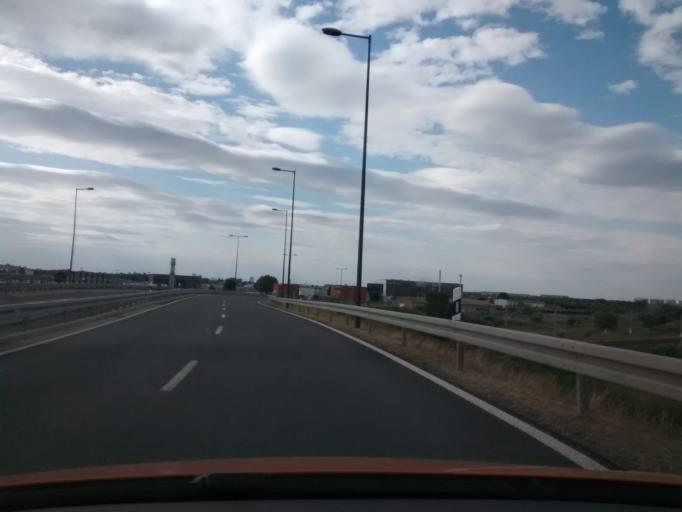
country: DE
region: Brandenburg
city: Schonefeld
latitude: 52.3709
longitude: 13.5332
